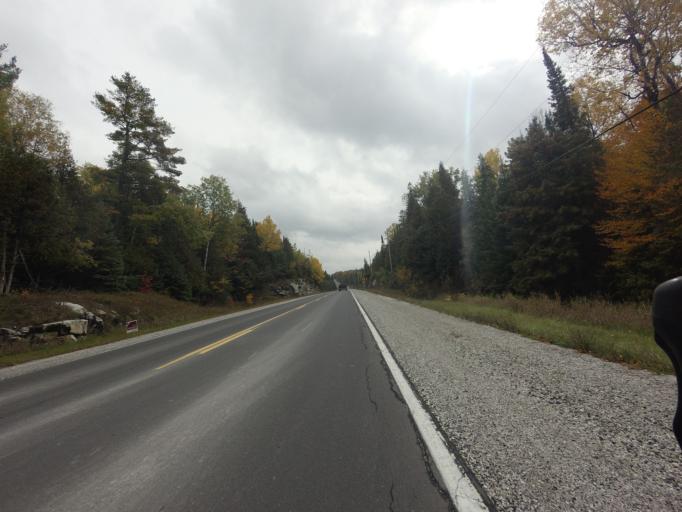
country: CA
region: Ontario
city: Perth
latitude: 45.1061
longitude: -76.4761
